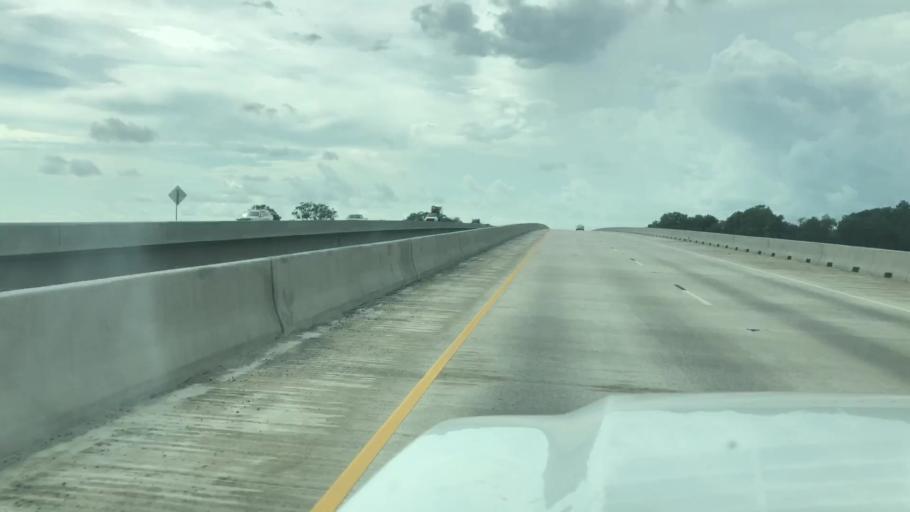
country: US
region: Louisiana
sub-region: Iberia Parish
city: Jeanerette
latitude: 29.8654
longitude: -91.6310
